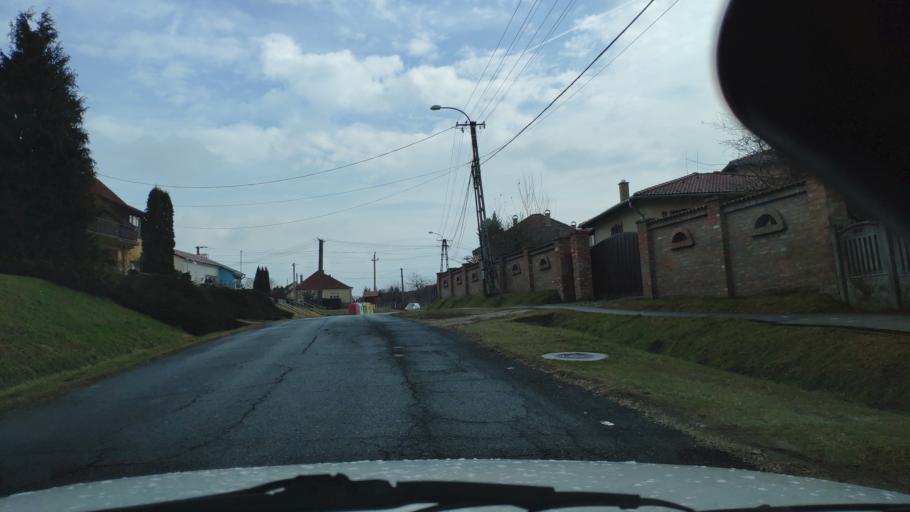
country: HU
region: Zala
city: Nagykanizsa
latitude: 46.4120
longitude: 16.9881
